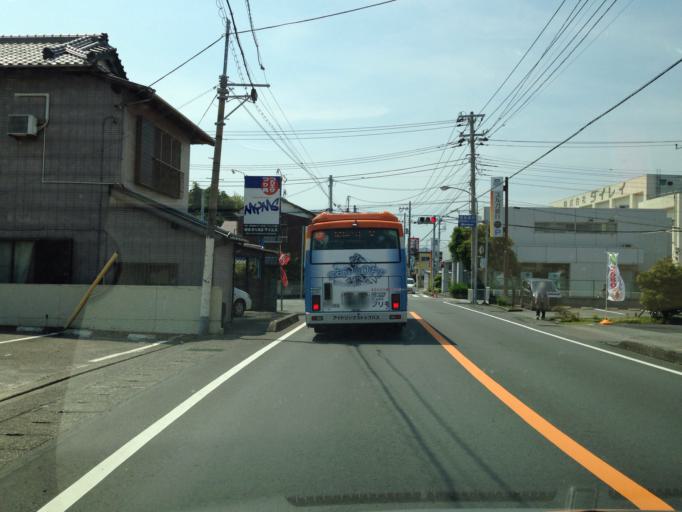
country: JP
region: Shizuoka
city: Numazu
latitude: 35.0621
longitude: 138.8801
